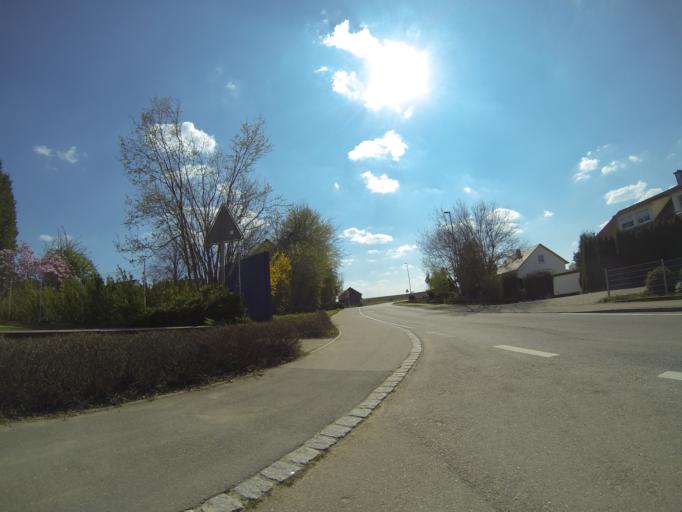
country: DE
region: Baden-Wuerttemberg
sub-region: Tuebingen Region
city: Burgrieden
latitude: 48.2319
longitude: 9.9272
